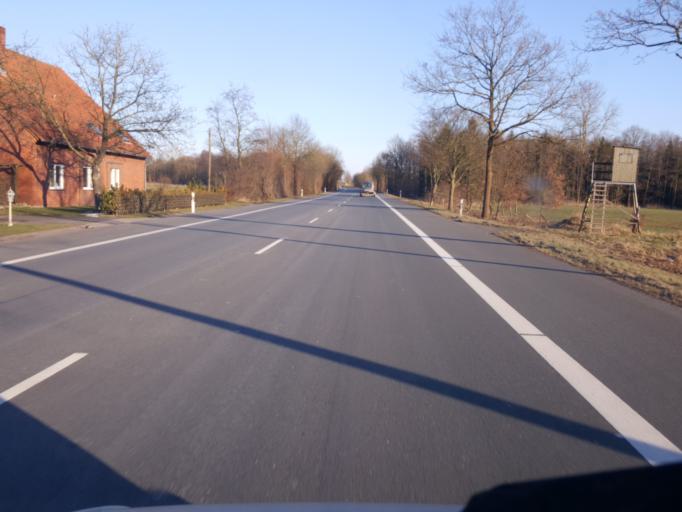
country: DE
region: North Rhine-Westphalia
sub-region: Regierungsbezirk Detmold
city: Hille
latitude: 52.3918
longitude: 8.7126
